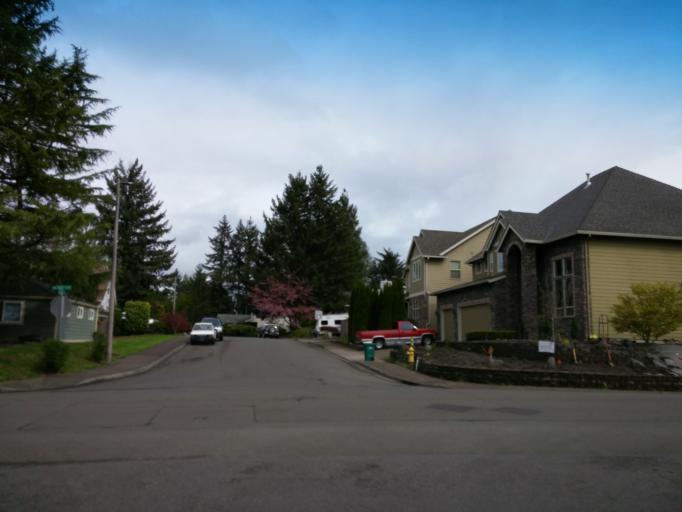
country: US
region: Oregon
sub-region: Washington County
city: Cedar Mill
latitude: 45.5199
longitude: -122.8315
